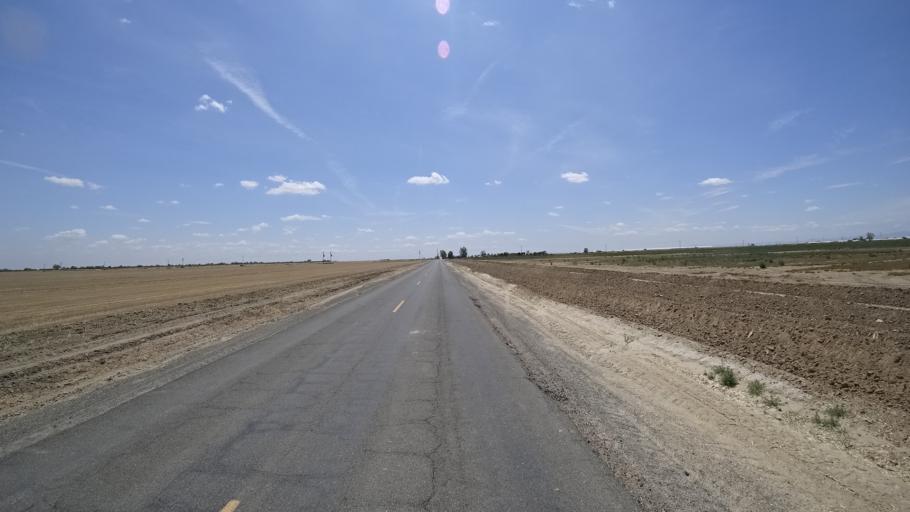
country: US
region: California
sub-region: Kings County
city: Home Garden
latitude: 36.2146
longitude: -119.6728
